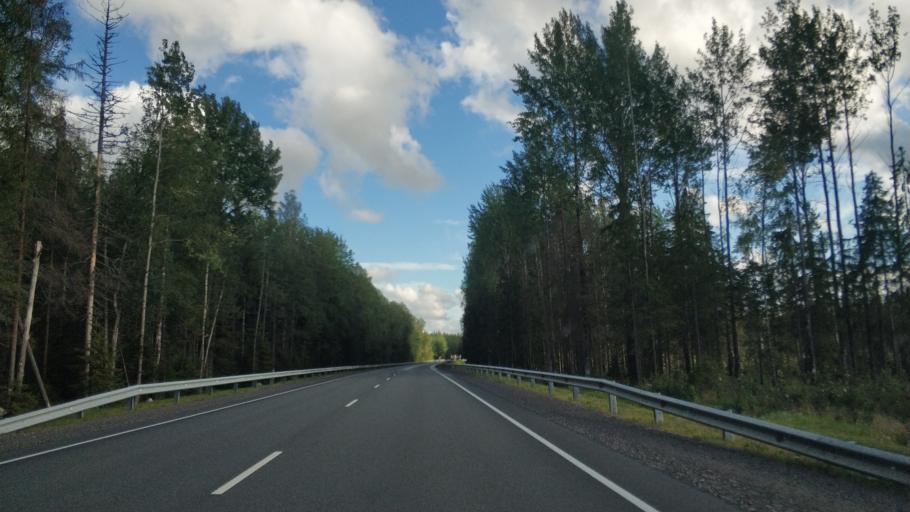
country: RU
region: Leningrad
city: Priozersk
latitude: 60.9131
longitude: 30.1574
